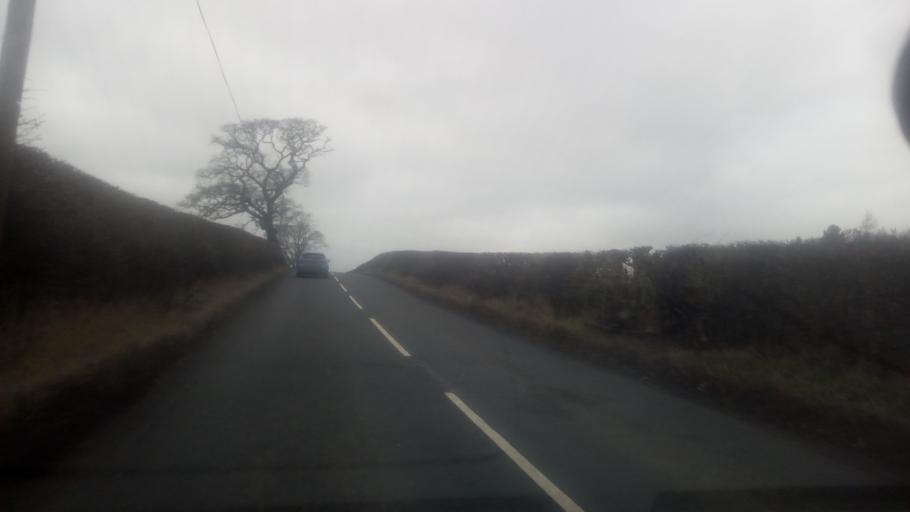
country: GB
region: Scotland
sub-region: The Scottish Borders
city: Kelso
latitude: 55.5810
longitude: -2.5007
